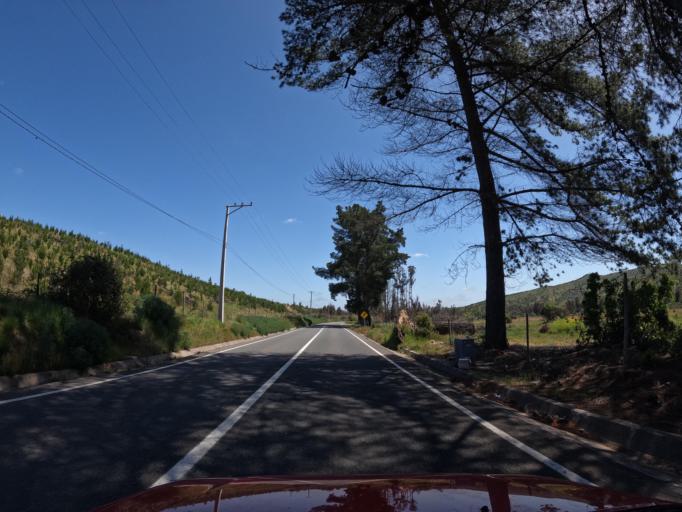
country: CL
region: O'Higgins
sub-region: Provincia de Colchagua
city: Santa Cruz
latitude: -34.6649
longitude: -71.8323
